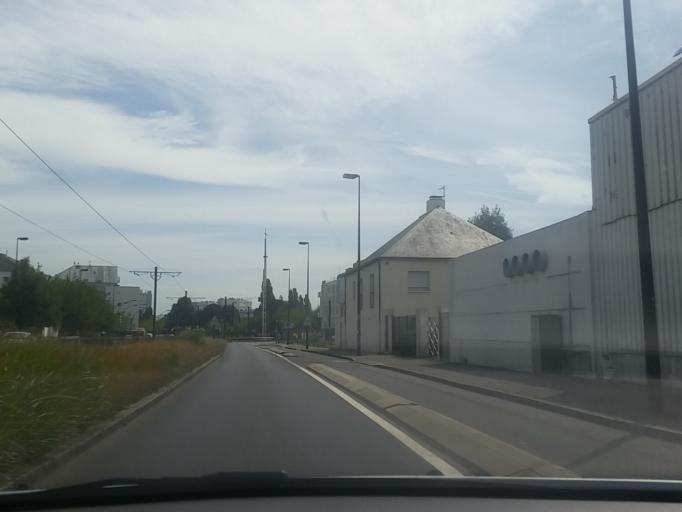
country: FR
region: Pays de la Loire
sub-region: Departement de la Loire-Atlantique
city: Bouguenais
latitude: 47.2096
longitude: -1.5988
